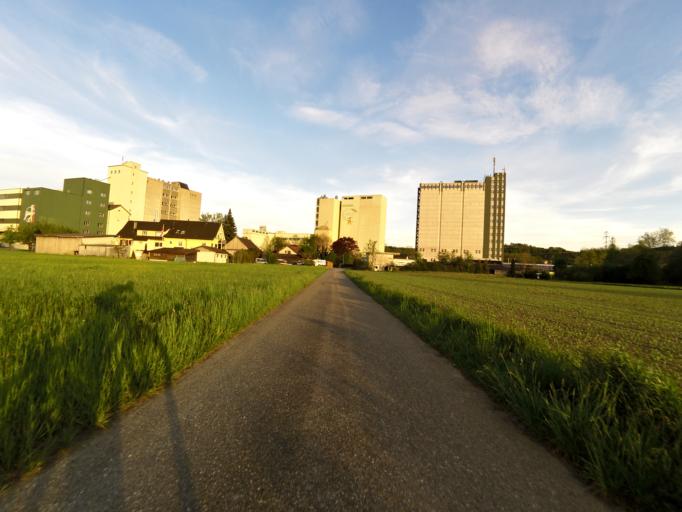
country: CH
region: Thurgau
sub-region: Frauenfeld District
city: Mullheim
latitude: 47.5899
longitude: 9.0095
